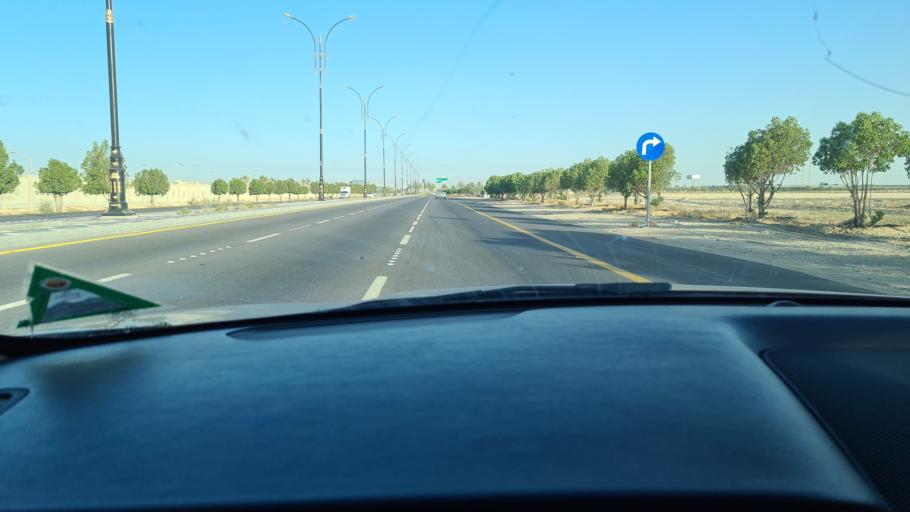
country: SA
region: Eastern Province
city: Al Jubayl
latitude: 26.9319
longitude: 49.7080
